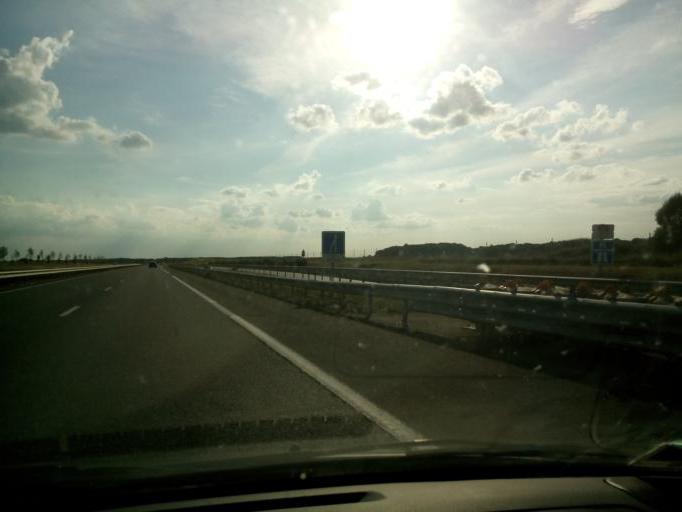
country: FR
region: Centre
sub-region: Departement d'Indre-et-Loire
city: Artannes-sur-Indre
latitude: 47.3077
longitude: 0.5701
